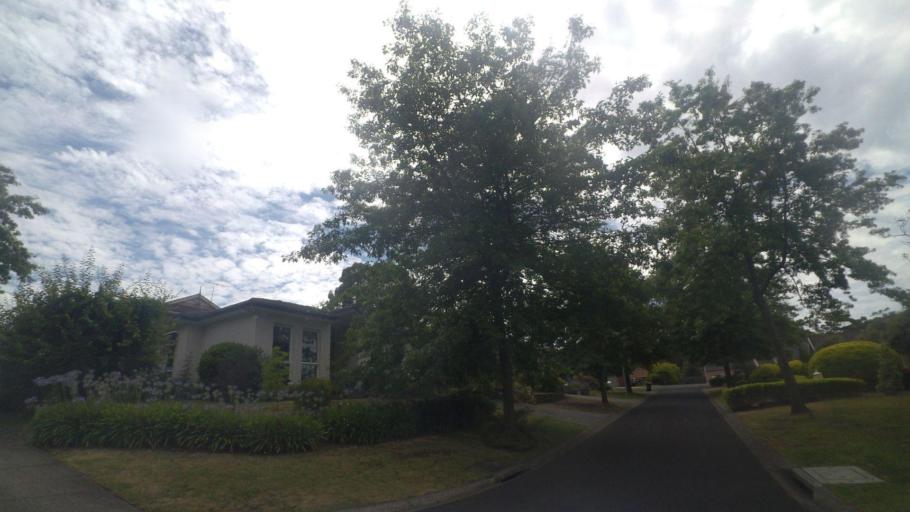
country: AU
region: Victoria
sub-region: Banyule
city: Viewbank
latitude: -37.7427
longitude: 145.0922
